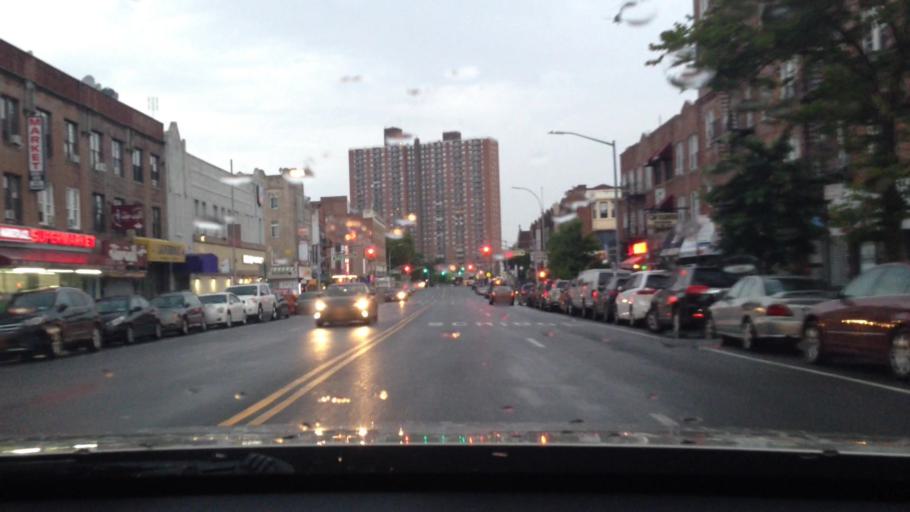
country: US
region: New York
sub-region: Kings County
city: Bensonhurst
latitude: 40.6338
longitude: -74.0238
